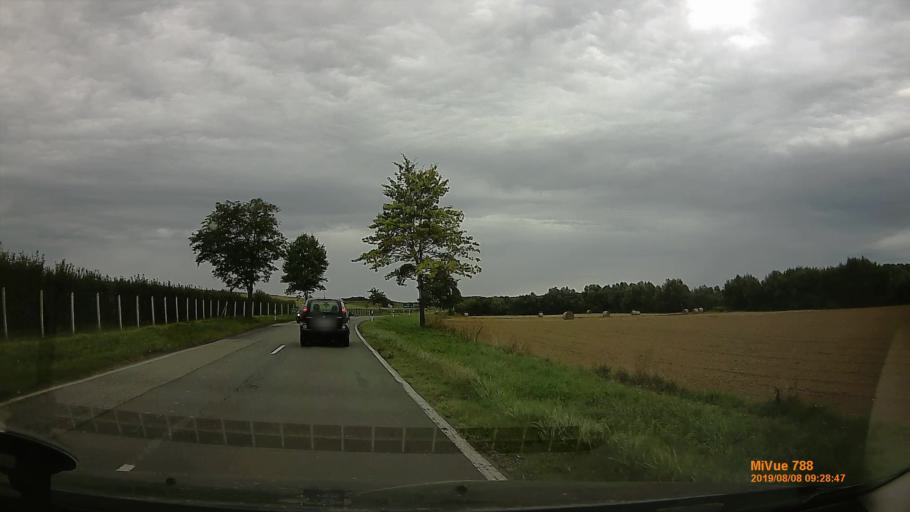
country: HU
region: Vas
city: Vasvar
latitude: 46.9669
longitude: 16.8429
